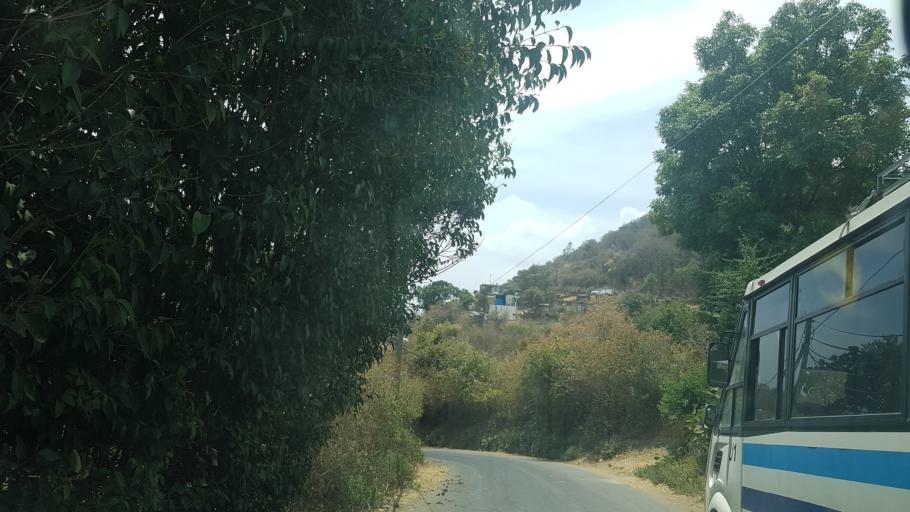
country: MX
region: Puebla
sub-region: Tochimilco
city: Santa Cruz Cuautomatitla
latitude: 18.8773
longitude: -98.6197
